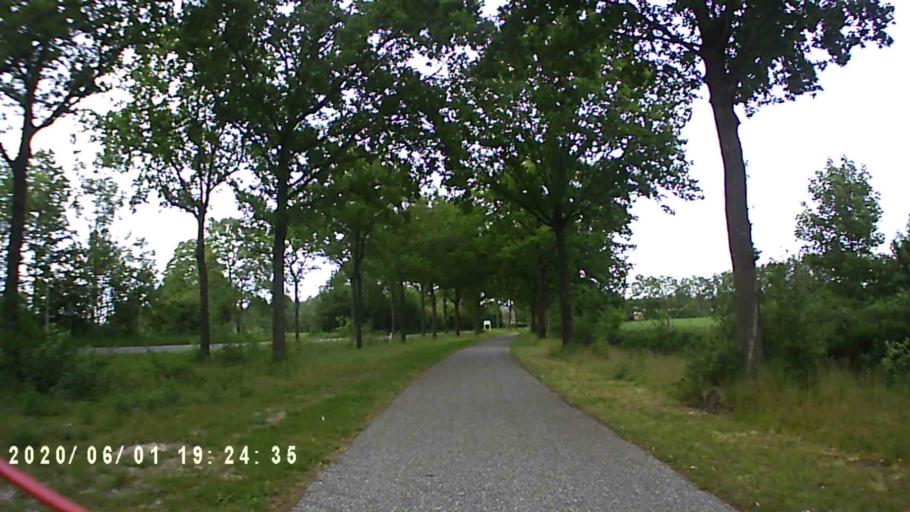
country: NL
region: Friesland
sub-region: Gemeente Achtkarspelen
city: Drogeham
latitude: 53.2063
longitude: 6.1291
